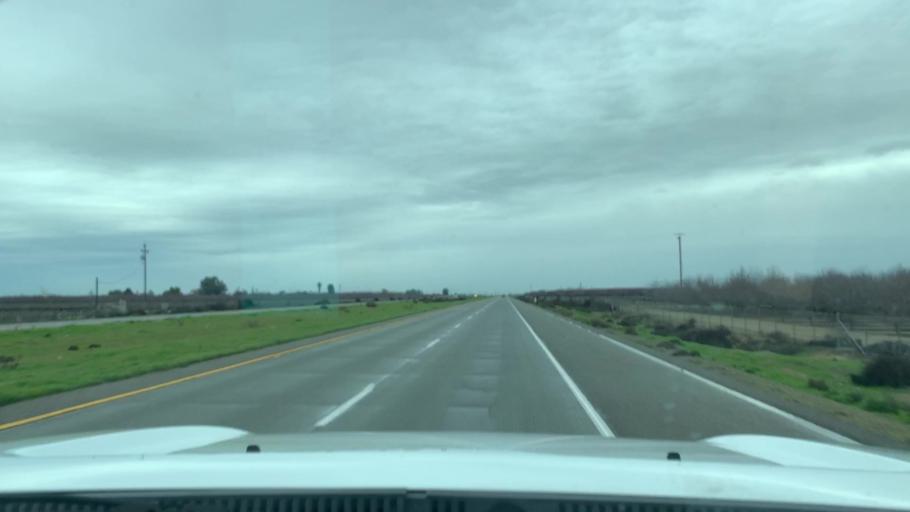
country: US
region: California
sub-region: Fresno County
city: Caruthers
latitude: 36.5354
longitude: -119.7860
